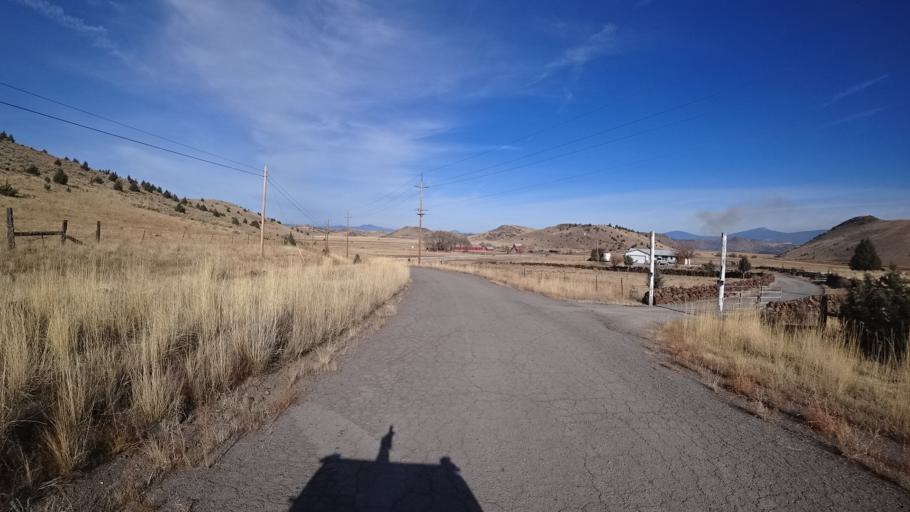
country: US
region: California
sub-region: Siskiyou County
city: Weed
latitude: 41.4978
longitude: -122.4552
